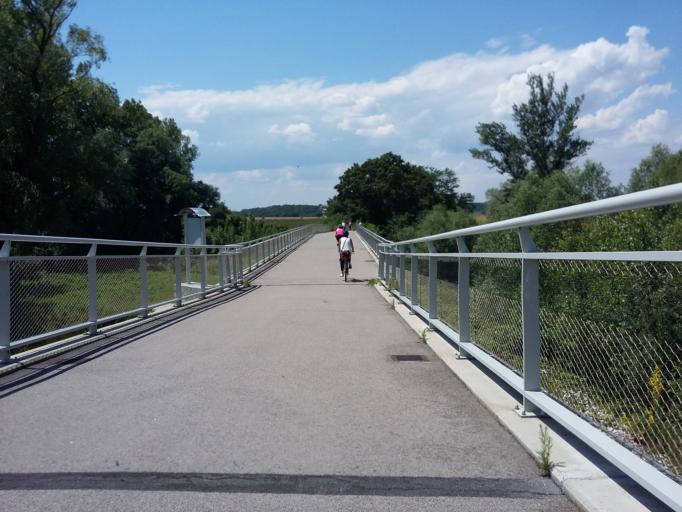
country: AT
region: Lower Austria
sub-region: Politischer Bezirk Bruck an der Leitha
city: Hainburg an der Donau
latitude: 48.2114
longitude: 16.9614
